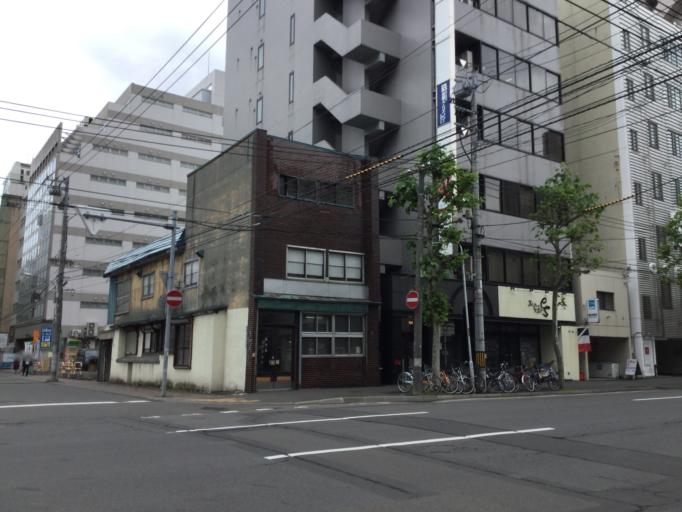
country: JP
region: Hokkaido
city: Sapporo
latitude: 43.0577
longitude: 141.3480
